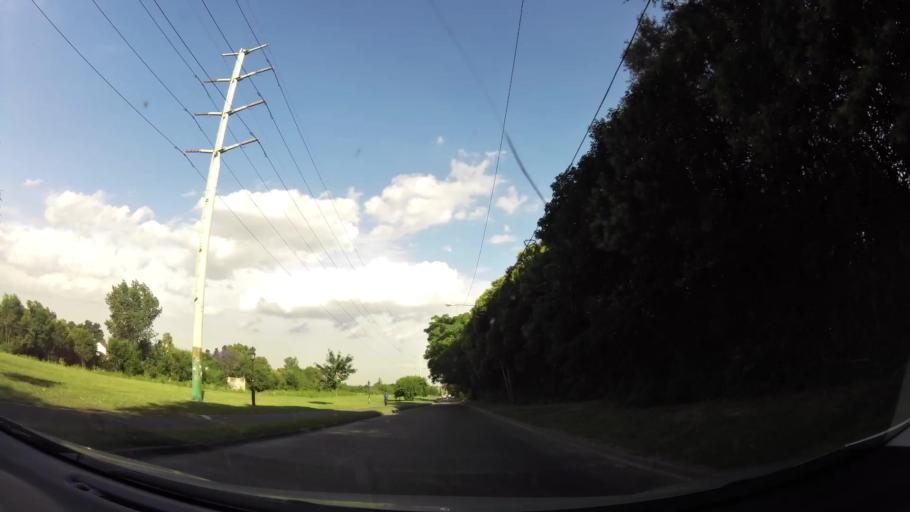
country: AR
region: Buenos Aires
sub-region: Partido de Tigre
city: Tigre
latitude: -34.4688
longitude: -58.6322
